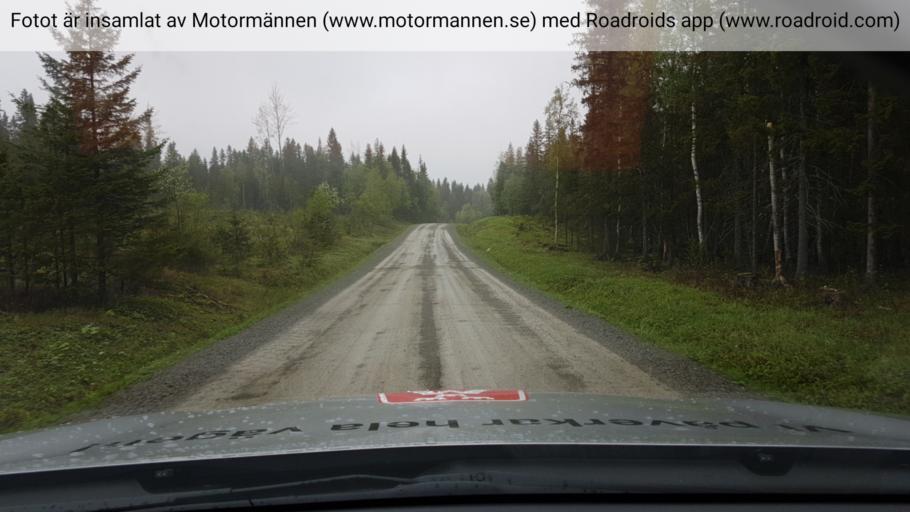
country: SE
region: Jaemtland
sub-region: Bergs Kommun
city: Hoverberg
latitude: 62.9728
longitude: 14.2214
